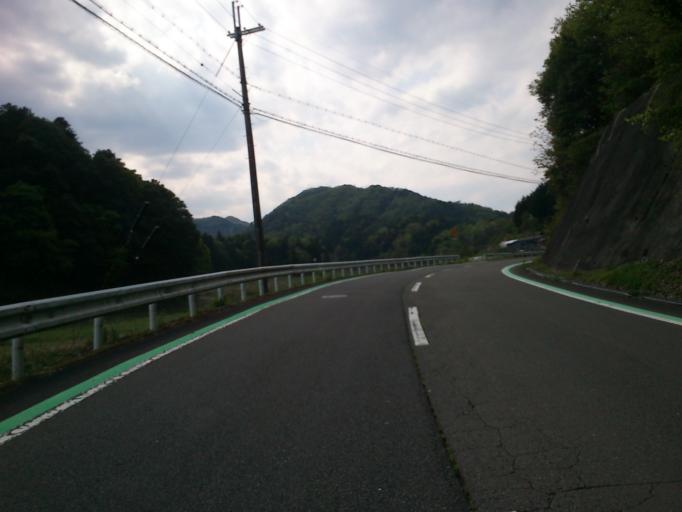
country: JP
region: Kyoto
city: Fukuchiyama
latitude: 35.2830
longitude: 135.0348
